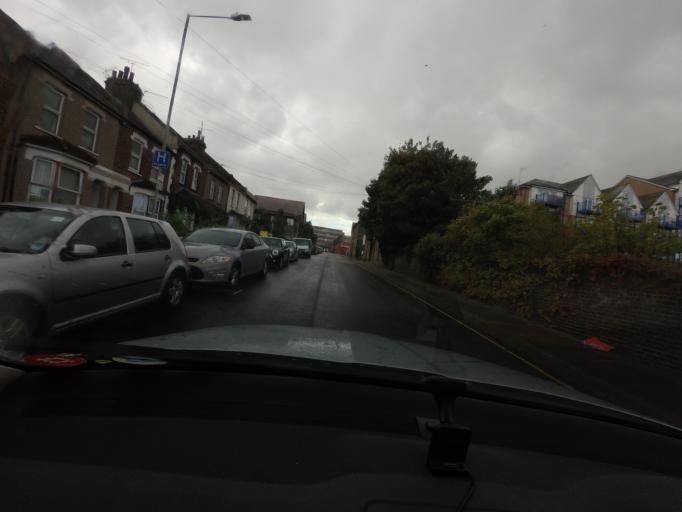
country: GB
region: England
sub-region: Kent
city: Gravesend
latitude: 51.4440
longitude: 0.3645
